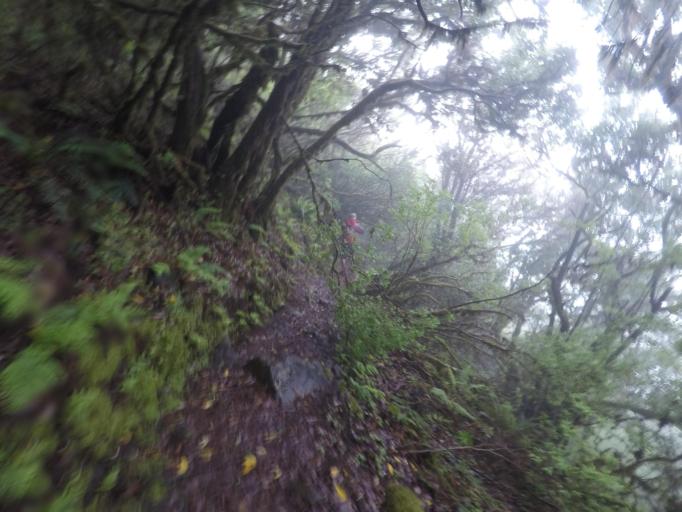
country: PT
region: Madeira
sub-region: Calheta
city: Arco da Calheta
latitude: 32.7738
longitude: -17.1214
